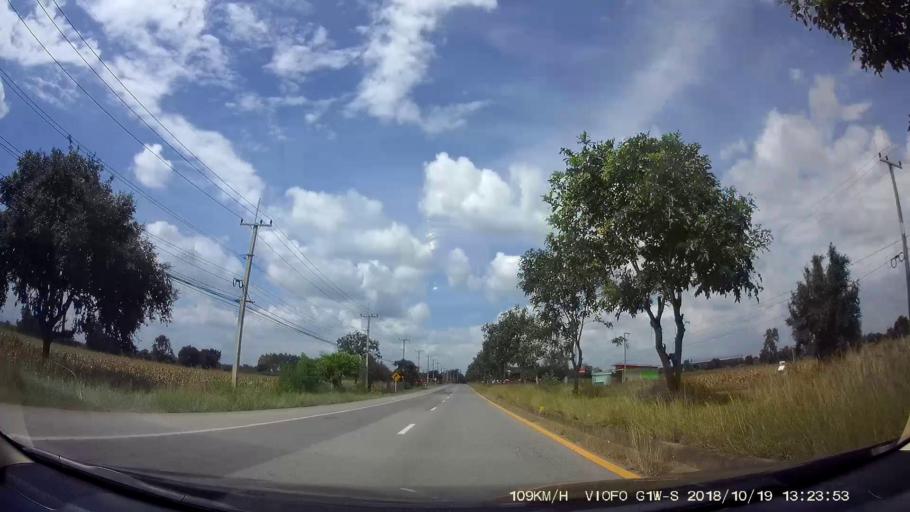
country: TH
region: Chaiyaphum
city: Chatturat
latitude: 15.4990
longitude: 101.8204
